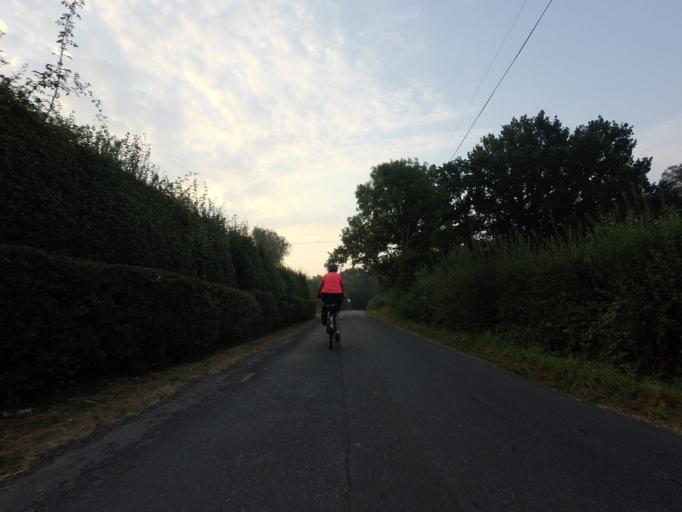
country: GB
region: England
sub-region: Kent
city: Lenham
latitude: 51.1892
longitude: 0.7079
